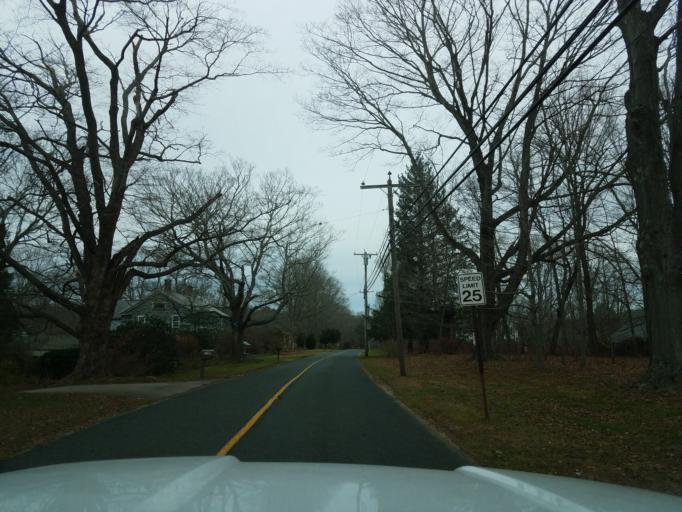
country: US
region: Connecticut
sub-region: New Haven County
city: North Branford
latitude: 41.3576
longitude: -72.7307
